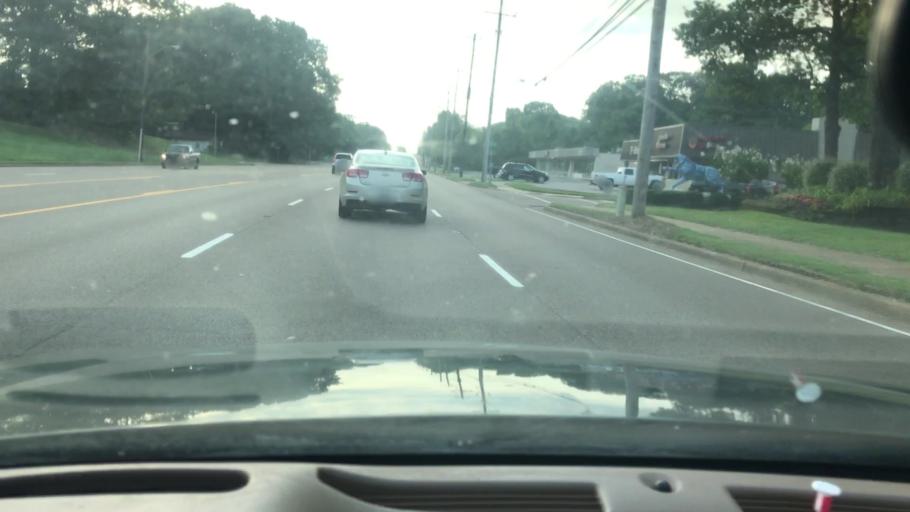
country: US
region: Tennessee
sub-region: Shelby County
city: Bartlett
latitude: 35.2047
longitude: -89.8539
